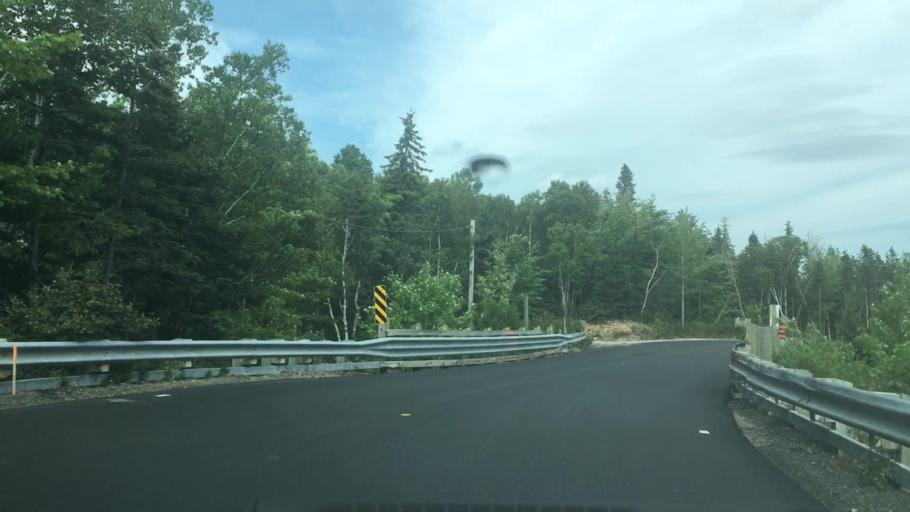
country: CA
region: Nova Scotia
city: Sydney Mines
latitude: 46.5463
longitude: -60.4153
